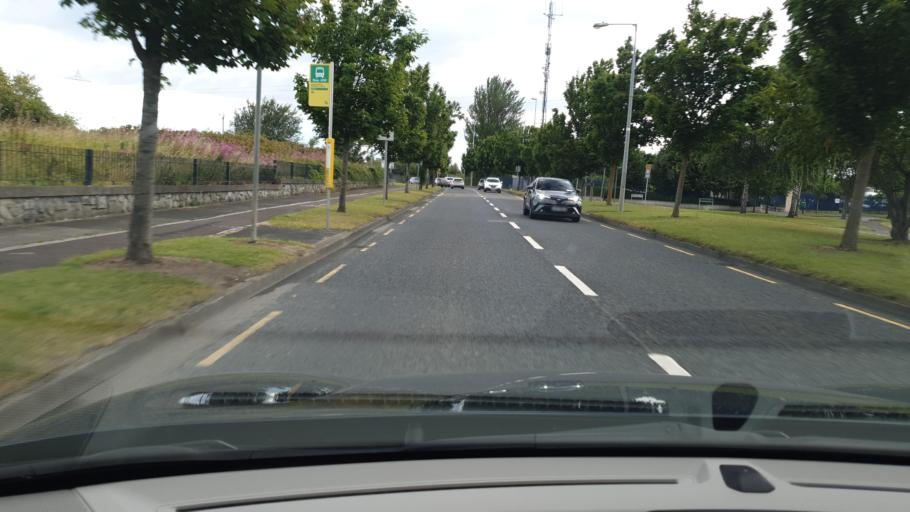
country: IE
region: Leinster
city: Clondalkin
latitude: 53.3369
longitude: -6.4053
